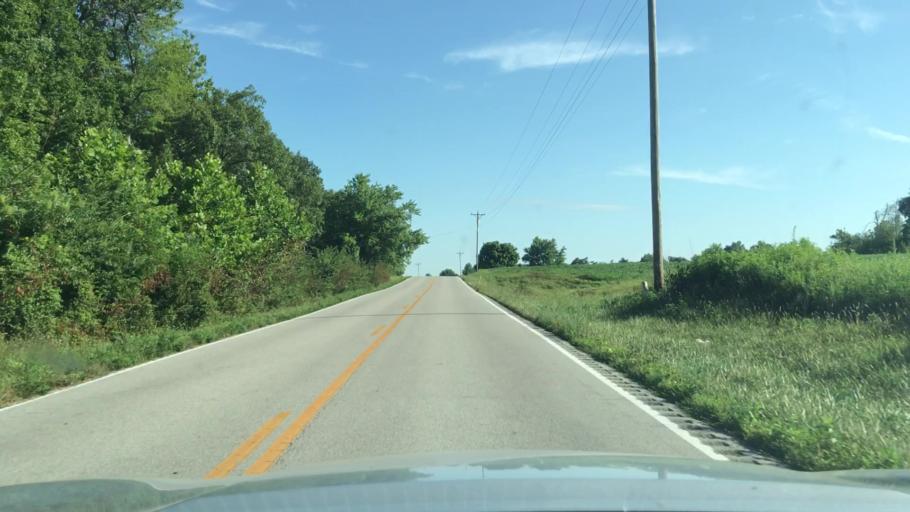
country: US
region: Kentucky
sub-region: Todd County
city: Elkton
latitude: 37.0077
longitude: -87.1309
